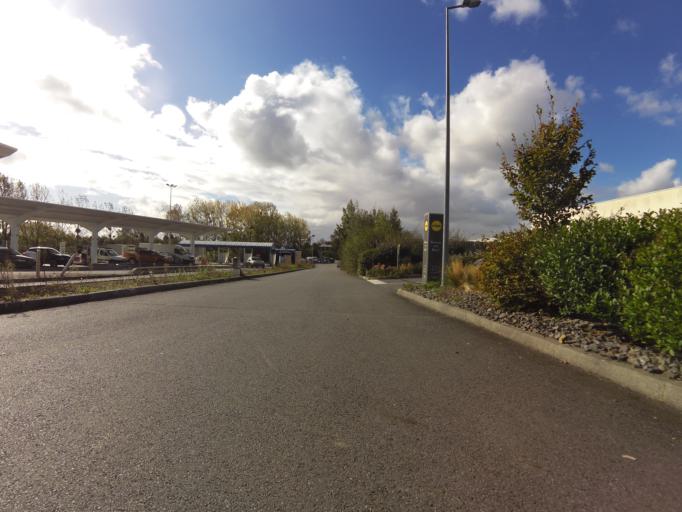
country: FR
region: Lower Normandy
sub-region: Departement de la Manche
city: Saint-Martin-des-Champs
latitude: 48.6532
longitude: -1.3496
